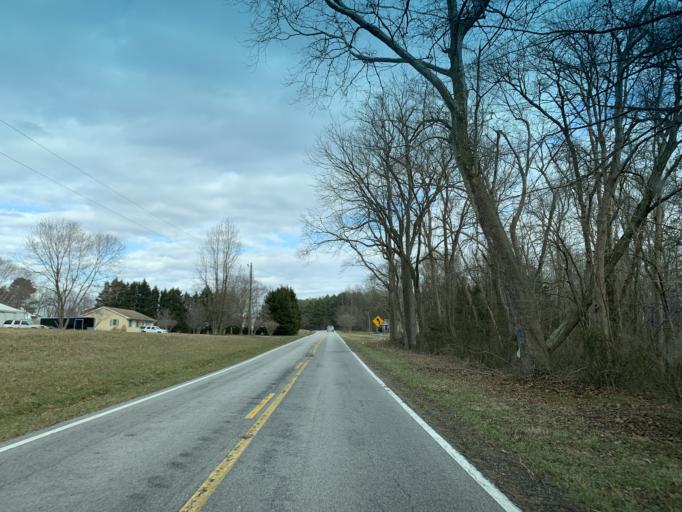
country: US
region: Maryland
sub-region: Caroline County
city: Ridgely
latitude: 38.9760
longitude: -75.9620
